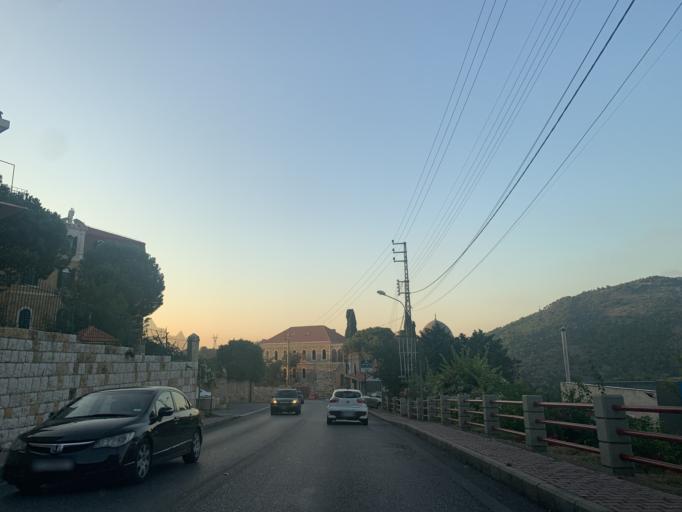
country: LB
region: Mont-Liban
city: Djounie
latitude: 33.9573
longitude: 35.6349
